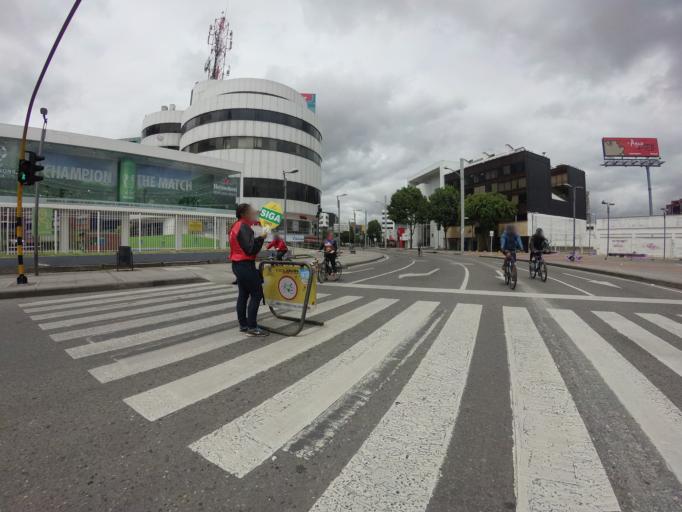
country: CO
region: Bogota D.C.
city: Barrio San Luis
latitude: 4.6843
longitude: -74.0482
